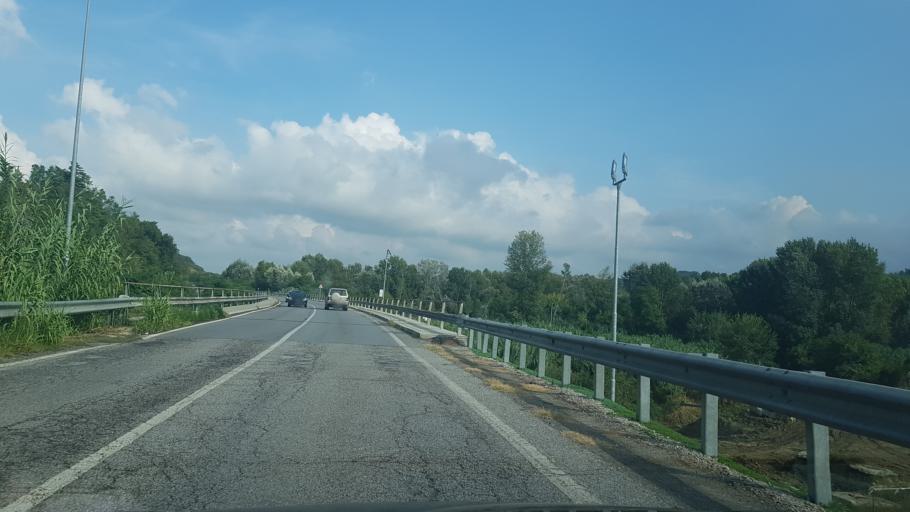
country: IT
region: Piedmont
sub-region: Provincia di Cuneo
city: Santo Stefano Belbo
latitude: 44.7116
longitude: 8.2462
